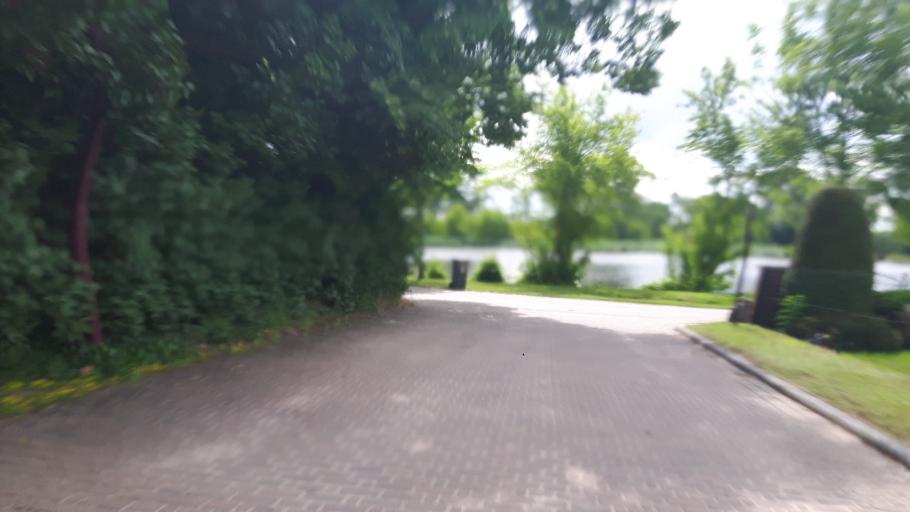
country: DE
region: Brandenburg
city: Mescherin
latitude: 53.2504
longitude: 14.4356
